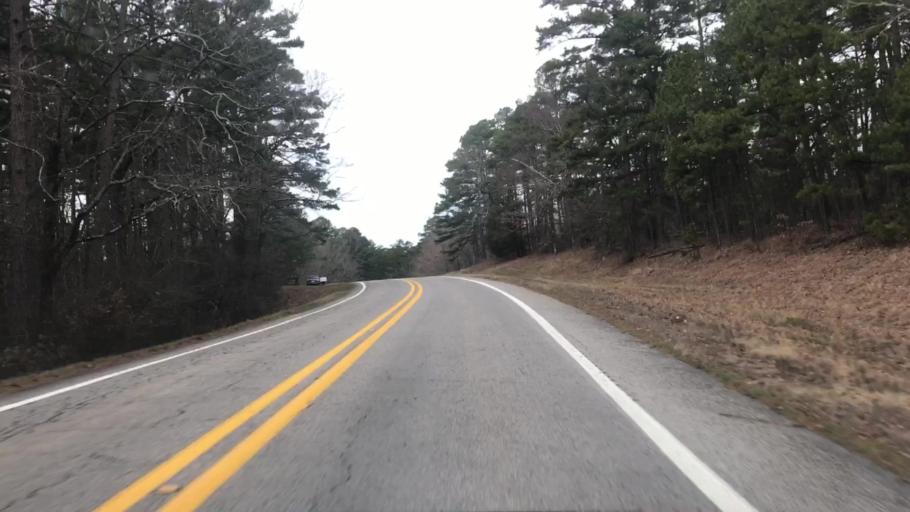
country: US
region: Arkansas
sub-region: Montgomery County
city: Mount Ida
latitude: 34.6709
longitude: -93.7808
